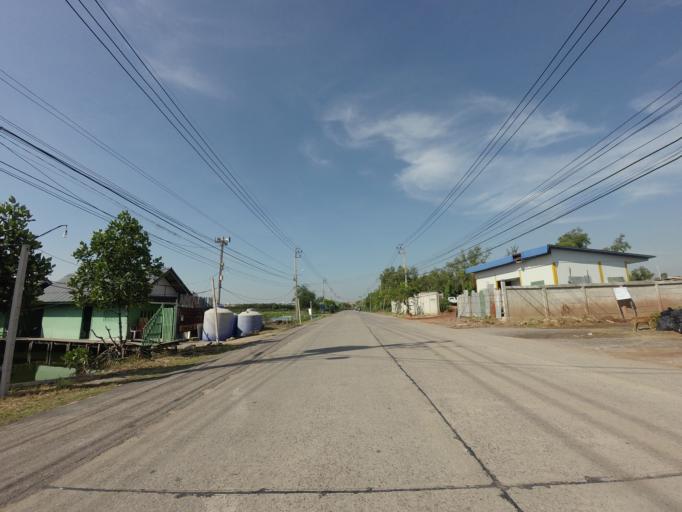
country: TH
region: Samut Prakan
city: Phra Samut Chedi
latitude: 13.5677
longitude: 100.5571
